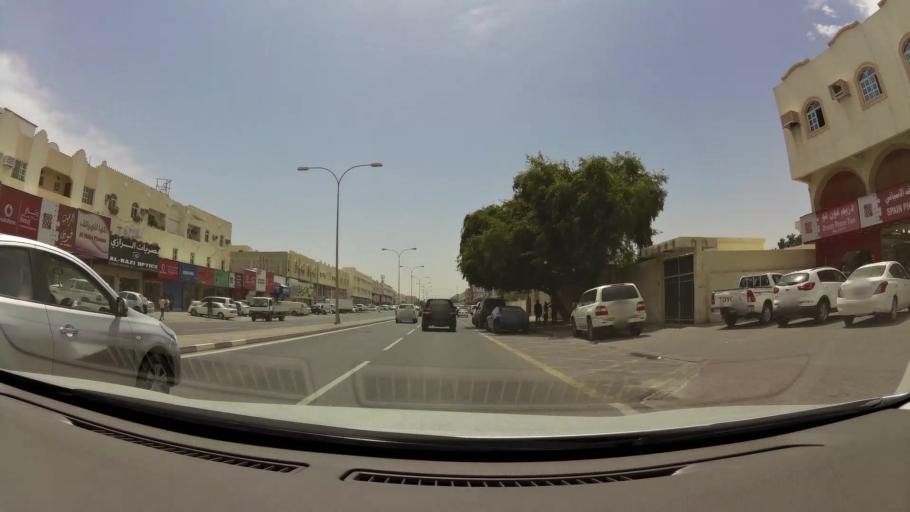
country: QA
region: Baladiyat ar Rayyan
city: Ar Rayyan
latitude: 25.2925
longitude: 51.4199
